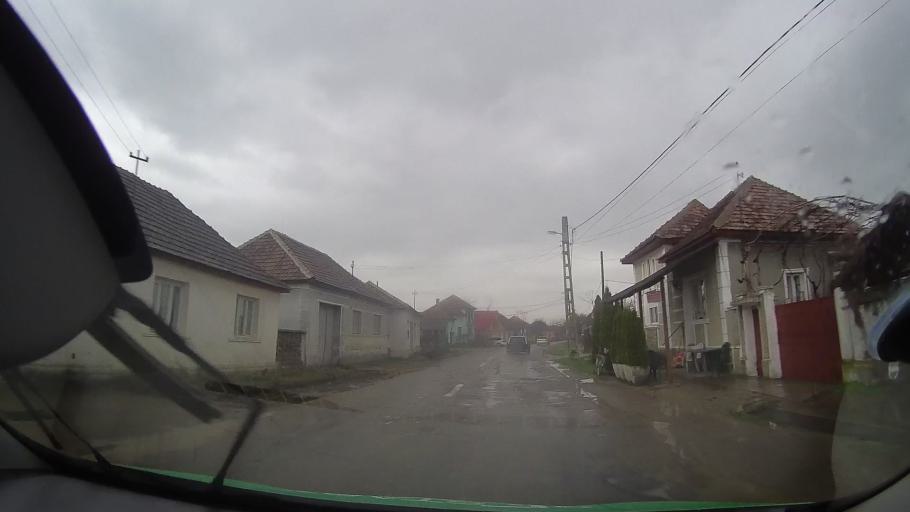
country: RO
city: Capalna
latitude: 46.7092
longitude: 22.0831
